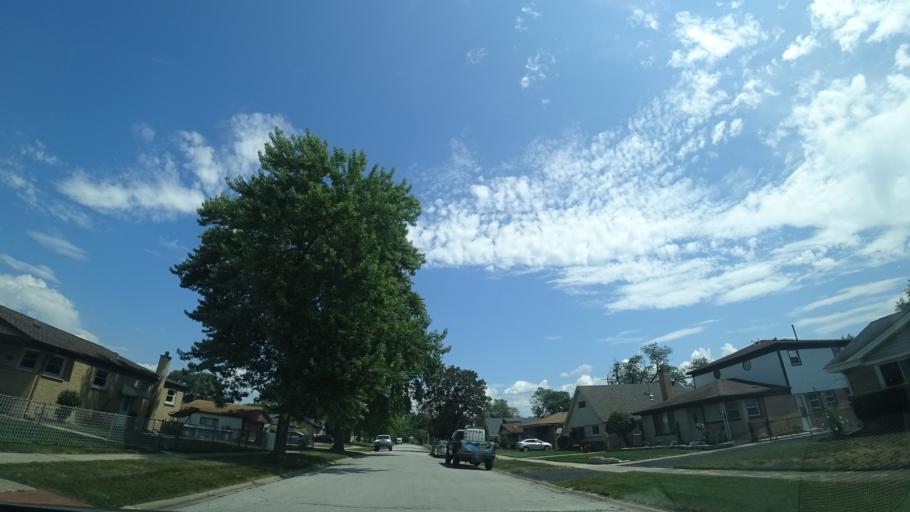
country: US
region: Illinois
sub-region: Cook County
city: Alsip
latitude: 41.6659
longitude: -87.7323
